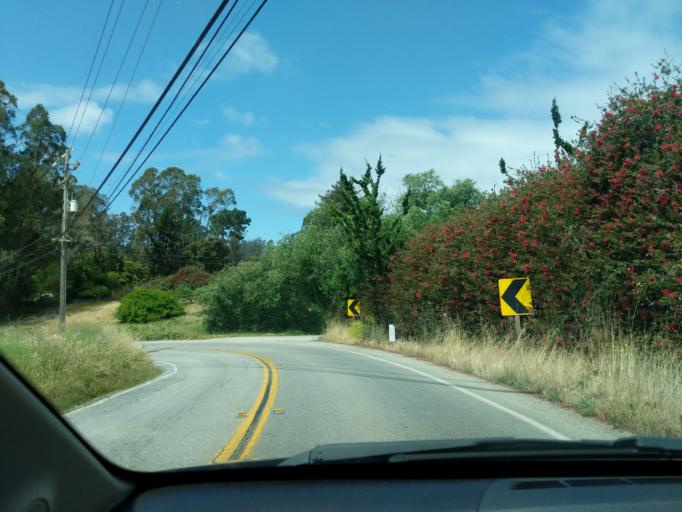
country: US
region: California
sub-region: Santa Cruz County
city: Freedom
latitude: 36.9402
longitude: -121.8029
